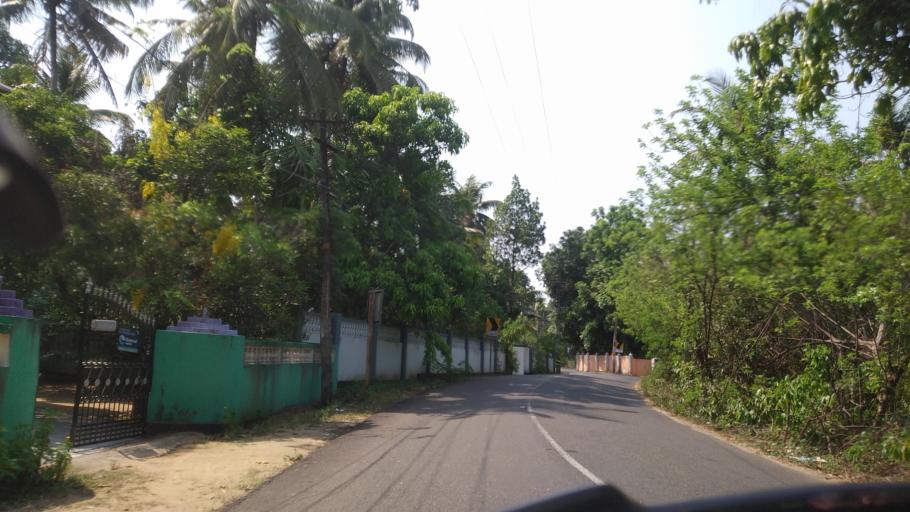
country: IN
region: Kerala
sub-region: Thrissur District
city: Thanniyam
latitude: 10.3345
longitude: 76.1198
